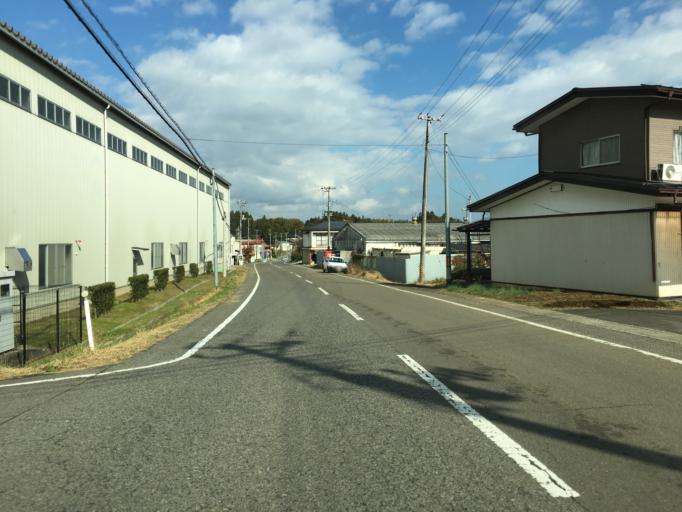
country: JP
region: Fukushima
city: Nihommatsu
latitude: 37.6411
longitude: 140.4765
